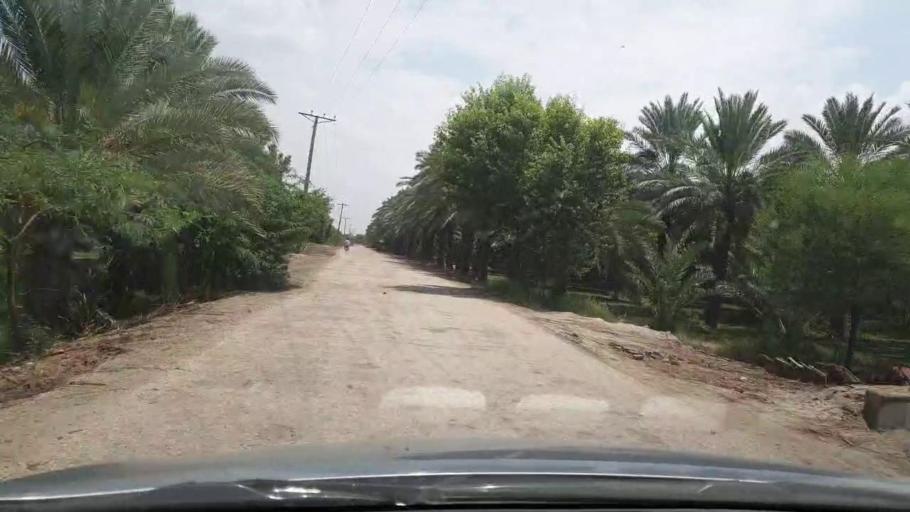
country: PK
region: Sindh
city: Khairpur
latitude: 27.4372
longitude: 68.7558
